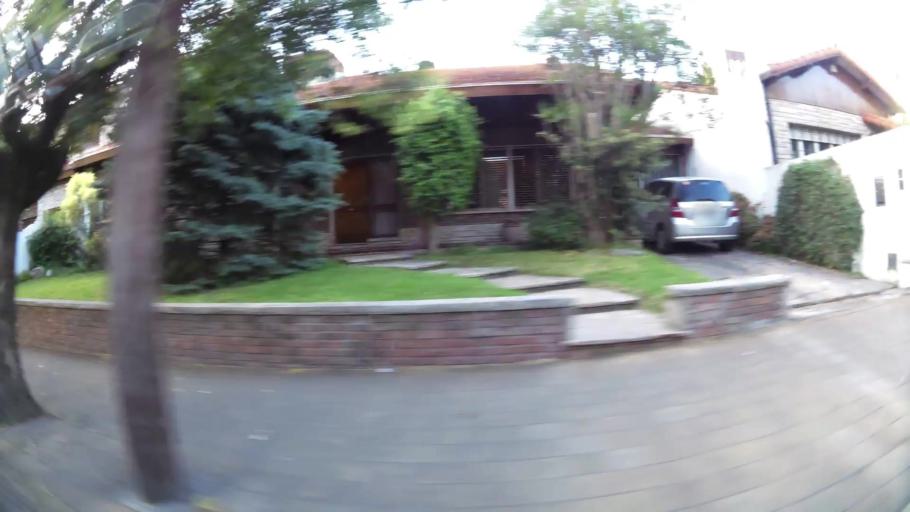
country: AR
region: Buenos Aires
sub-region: Partido de Vicente Lopez
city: Olivos
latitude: -34.5393
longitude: -58.5011
